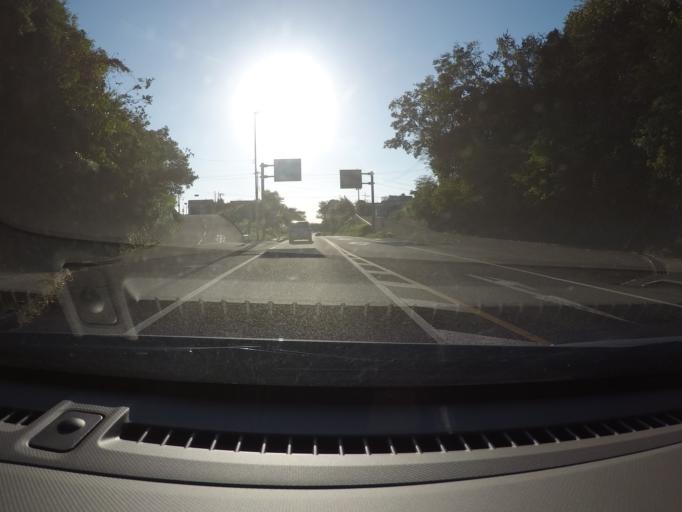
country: JP
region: Kagoshima
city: Izumi
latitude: 32.1320
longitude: 130.3493
